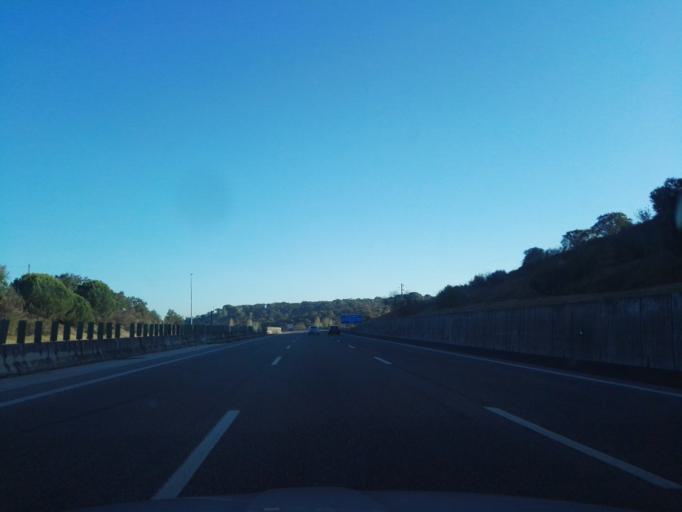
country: PT
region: Lisbon
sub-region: Alenquer
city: Carregado
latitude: 39.0509
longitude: -8.9451
